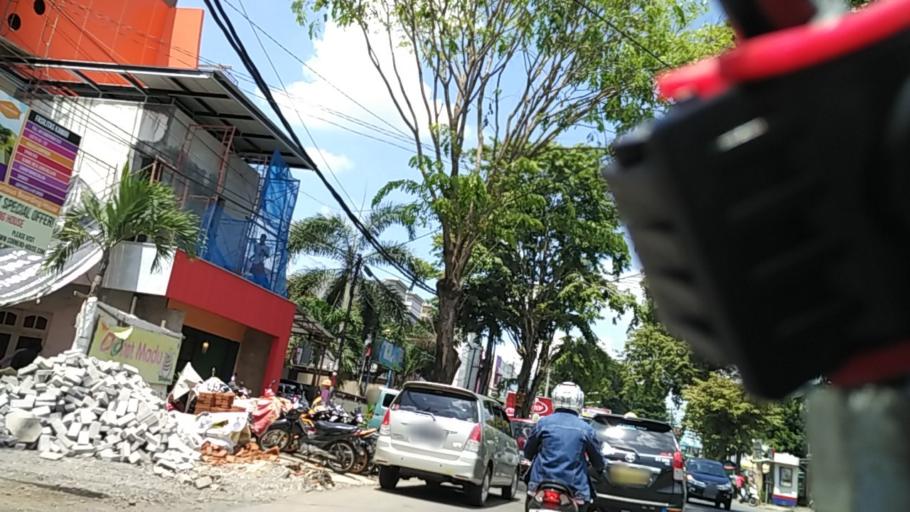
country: ID
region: Central Java
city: Semarang
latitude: -7.0502
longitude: 110.4230
